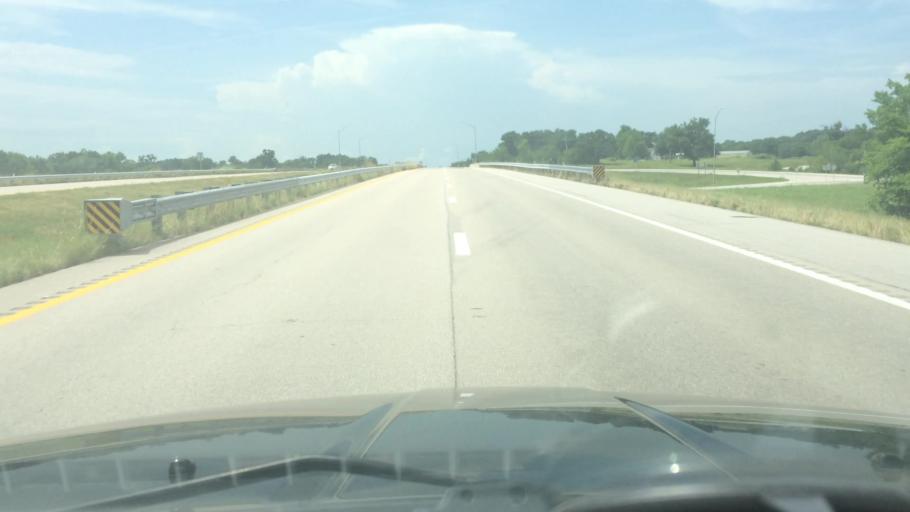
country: US
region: Missouri
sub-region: Polk County
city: Humansville
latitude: 37.7929
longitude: -93.5872
